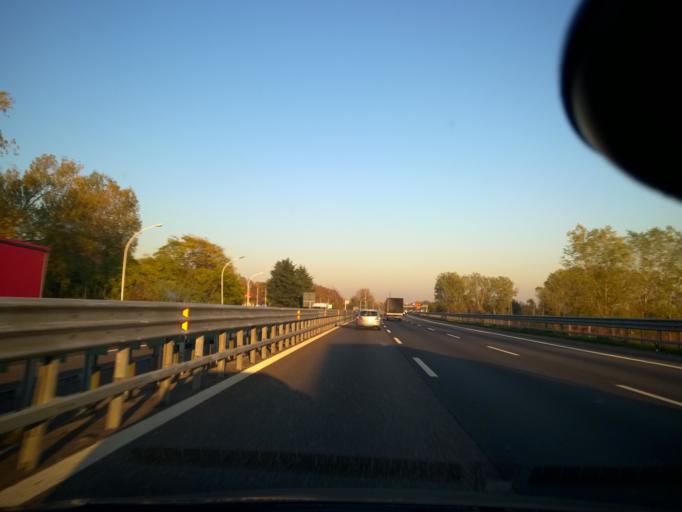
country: IT
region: Lombardy
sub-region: Citta metropolitana di Milano
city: Fizzonasco
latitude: 45.3906
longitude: 9.1882
